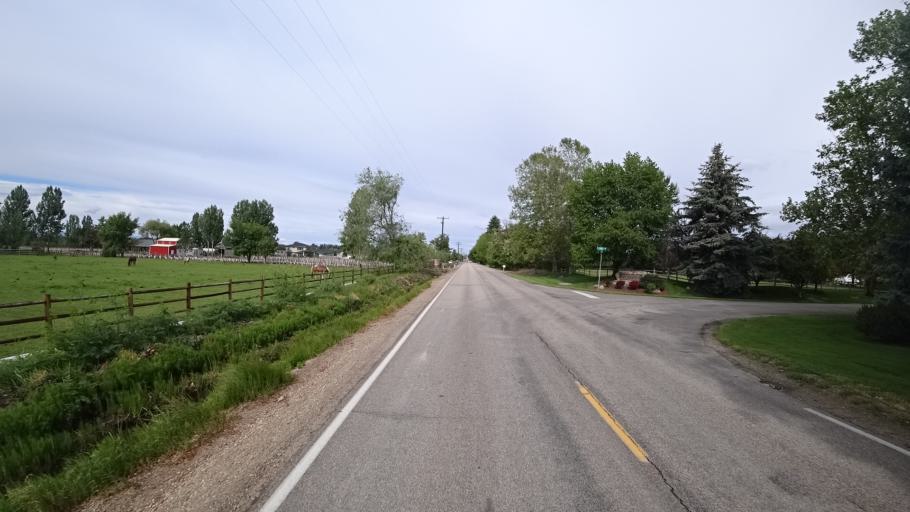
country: US
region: Idaho
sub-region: Ada County
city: Eagle
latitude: 43.7208
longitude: -116.3963
